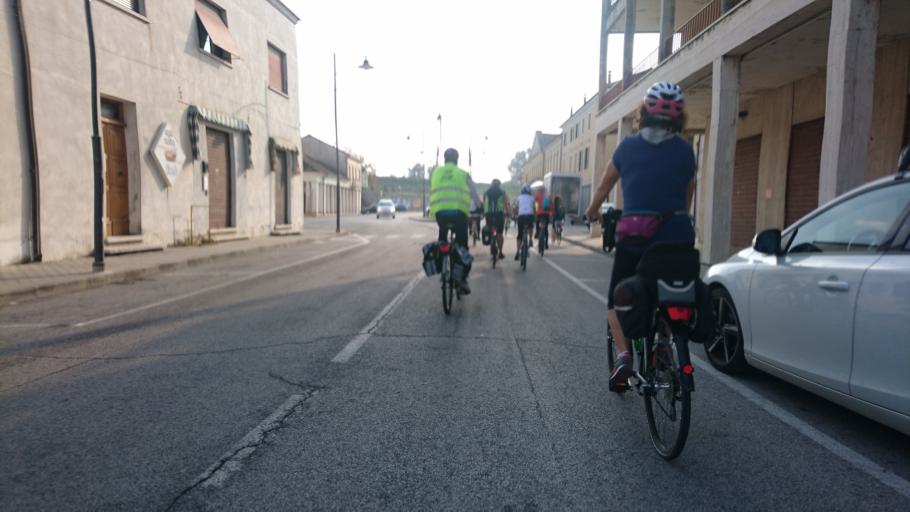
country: IT
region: Veneto
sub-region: Provincia di Rovigo
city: Polesella
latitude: 44.9620
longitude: 11.7547
